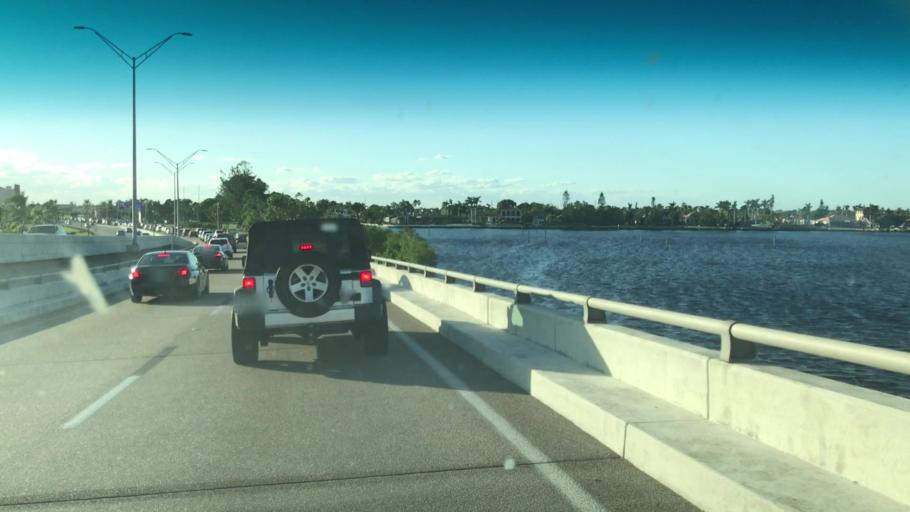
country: US
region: Florida
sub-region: Lee County
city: McGregor
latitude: 26.5622
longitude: -81.9317
